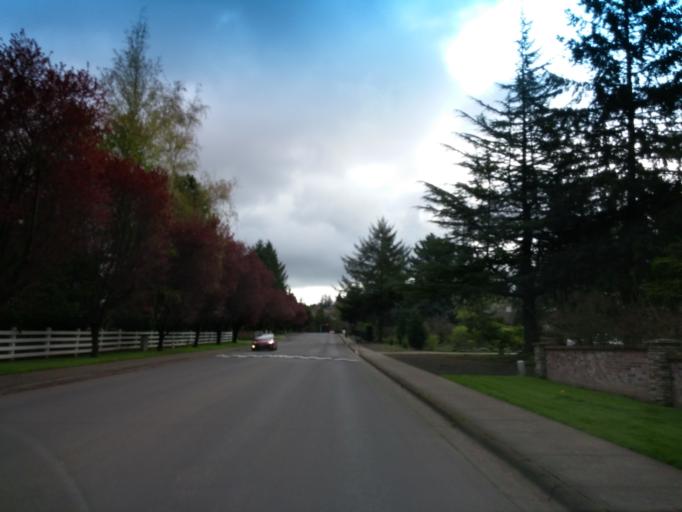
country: US
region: Oregon
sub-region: Washington County
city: Cedar Mill
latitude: 45.5369
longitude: -122.8163
